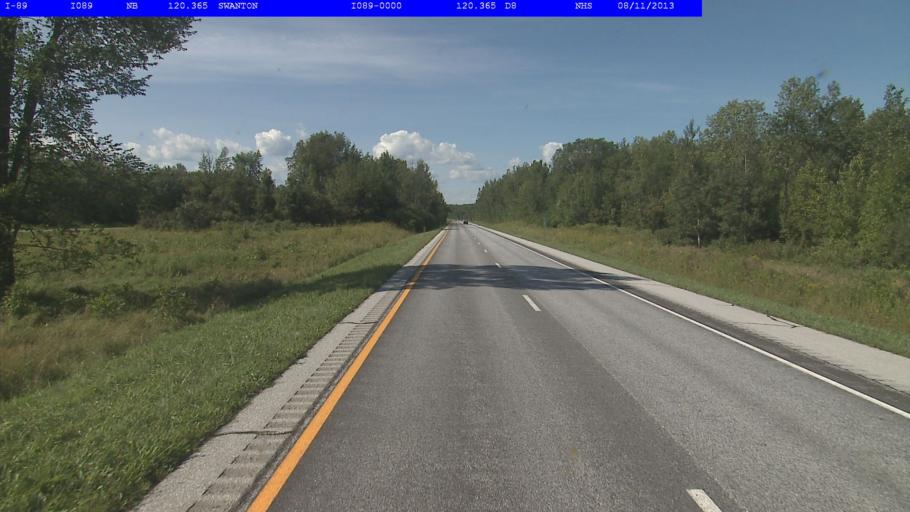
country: US
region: Vermont
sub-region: Franklin County
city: Swanton
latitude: 44.8822
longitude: -73.0843
